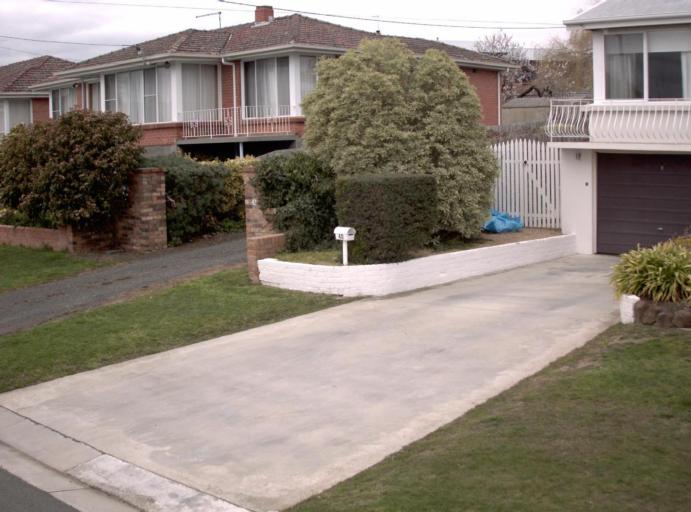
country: AU
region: Tasmania
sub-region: Launceston
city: Newstead
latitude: -41.4493
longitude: 147.1768
